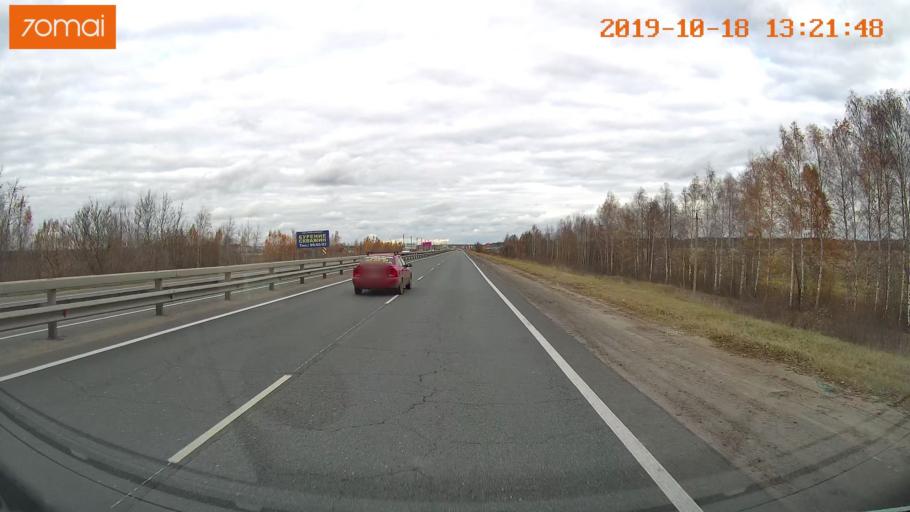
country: RU
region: Rjazan
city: Polyany
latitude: 54.7002
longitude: 39.8420
